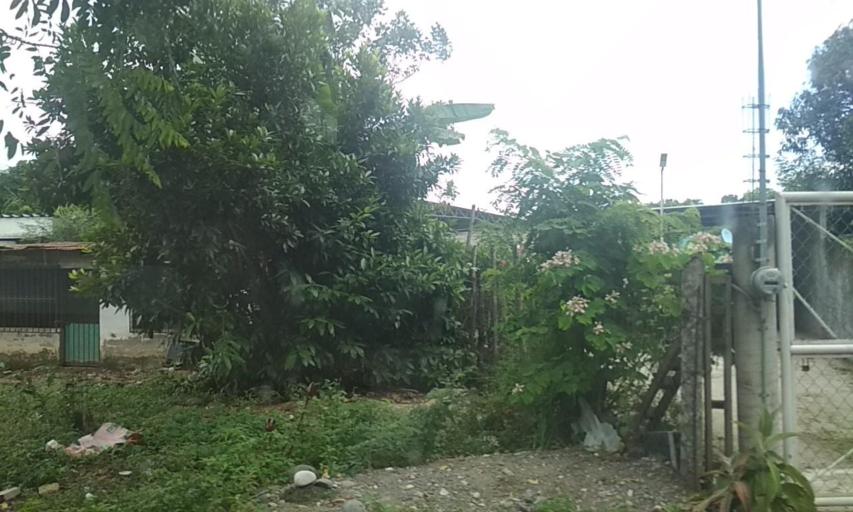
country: MX
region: Veracruz
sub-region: Martinez de la Torre
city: El Progreso
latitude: 20.0965
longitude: -97.0100
